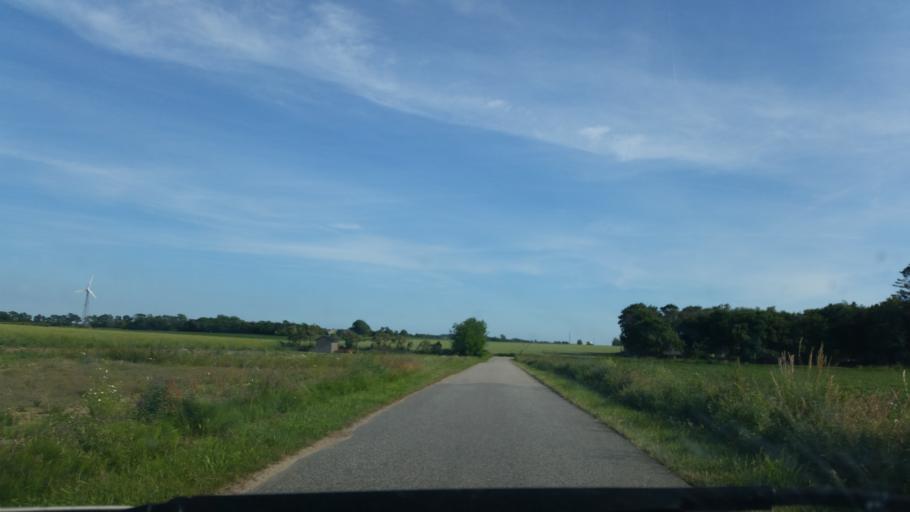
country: DK
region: Central Jutland
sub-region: Samso Kommune
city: Tranebjerg
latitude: 55.9682
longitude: 10.5577
